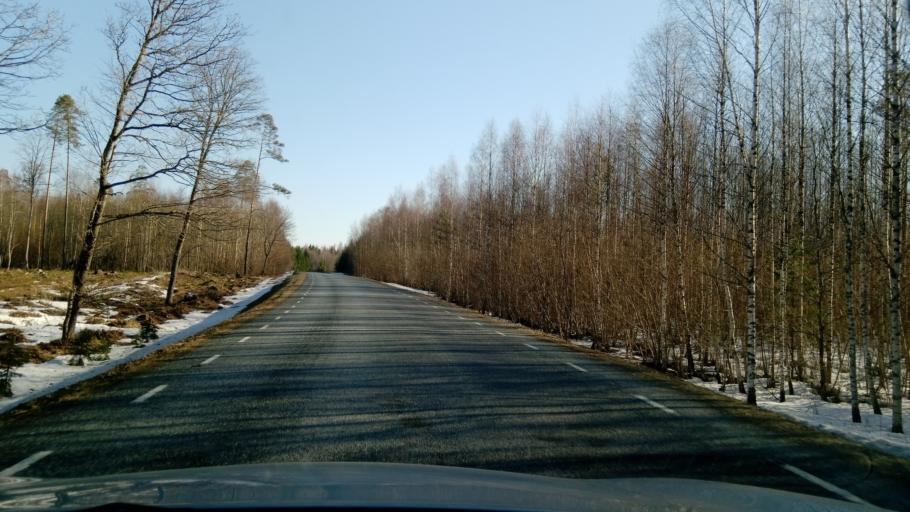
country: EE
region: Laeaene-Virumaa
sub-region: Kadrina vald
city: Kadrina
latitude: 59.2552
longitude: 26.2283
